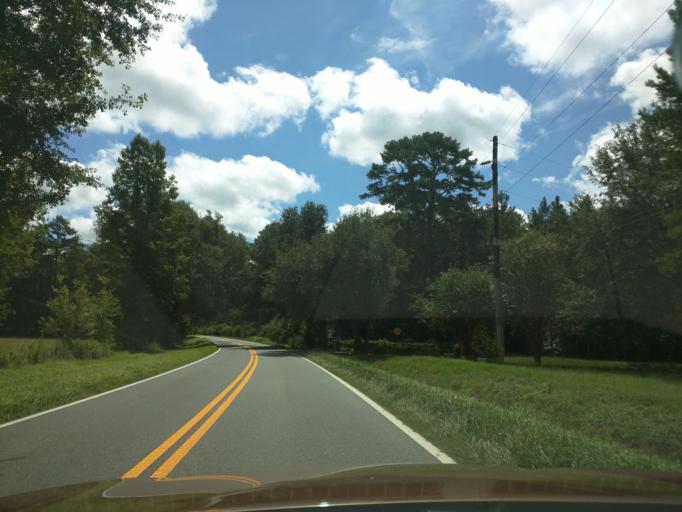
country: US
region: Florida
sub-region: Leon County
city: Tallahassee
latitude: 30.5363
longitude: -84.1729
